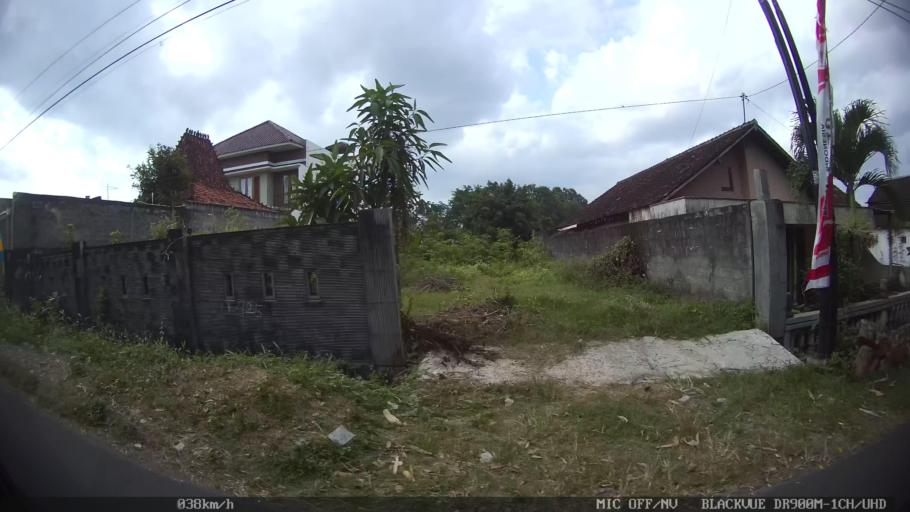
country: ID
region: Daerah Istimewa Yogyakarta
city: Gamping Lor
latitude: -7.7890
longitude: 110.3391
